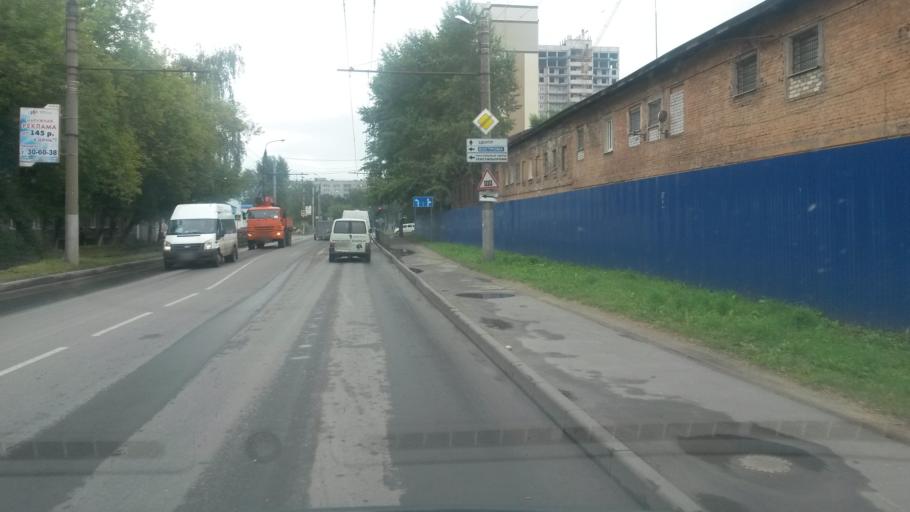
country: RU
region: Ivanovo
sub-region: Gorod Ivanovo
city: Ivanovo
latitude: 57.0078
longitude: 40.9481
